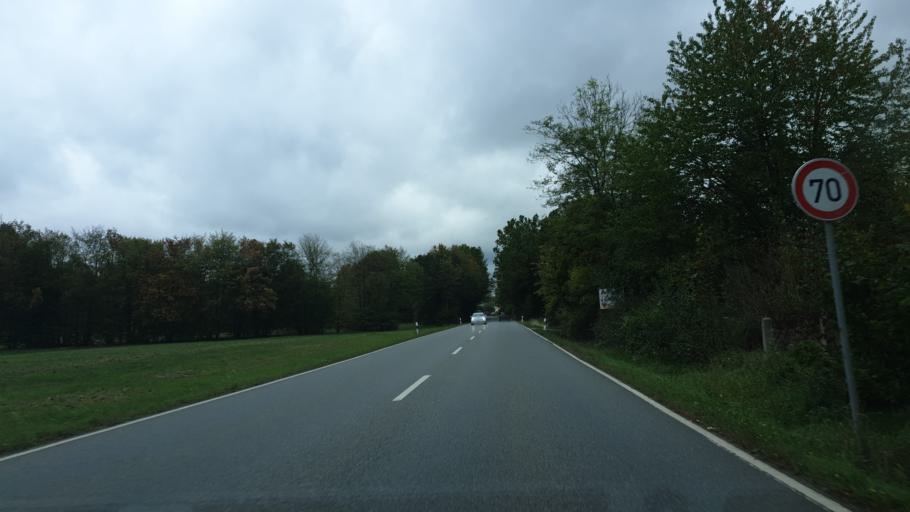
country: DE
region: Saxony
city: Glauchau
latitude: 50.8149
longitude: 12.5704
